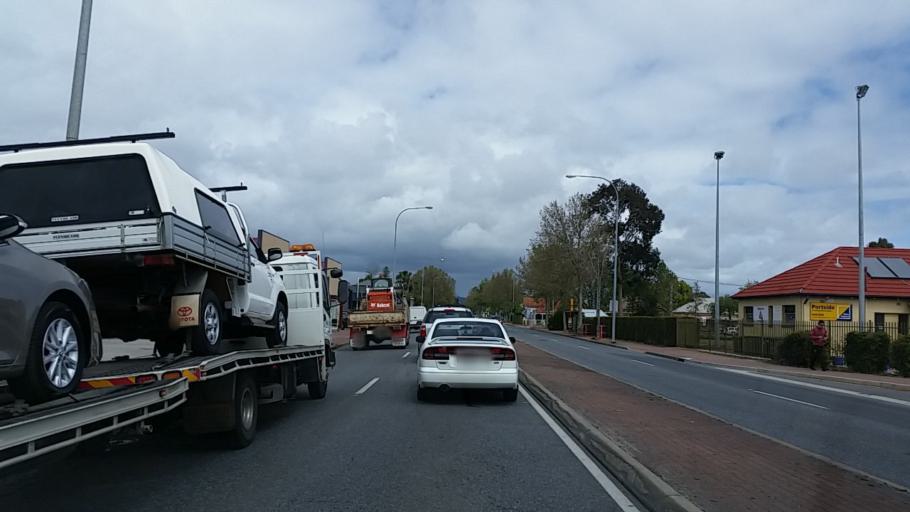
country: AU
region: South Australia
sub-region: City of West Torrens
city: Thebarton
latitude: -34.9165
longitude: 138.5670
